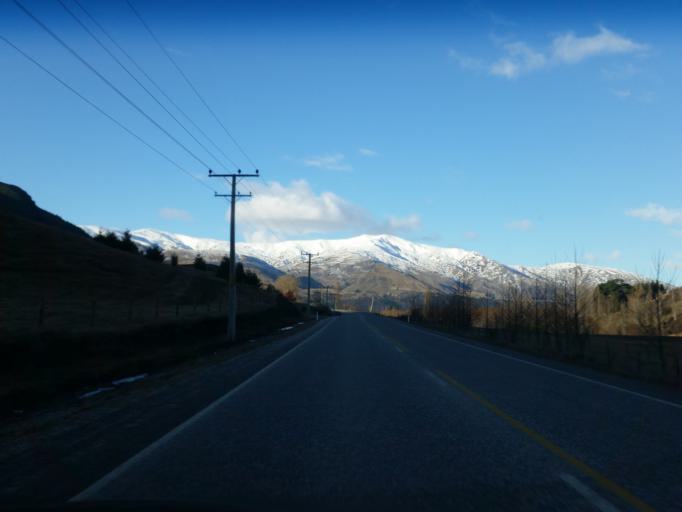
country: NZ
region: Otago
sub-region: Queenstown-Lakes District
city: Arrowtown
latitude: -44.9467
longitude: 168.7800
